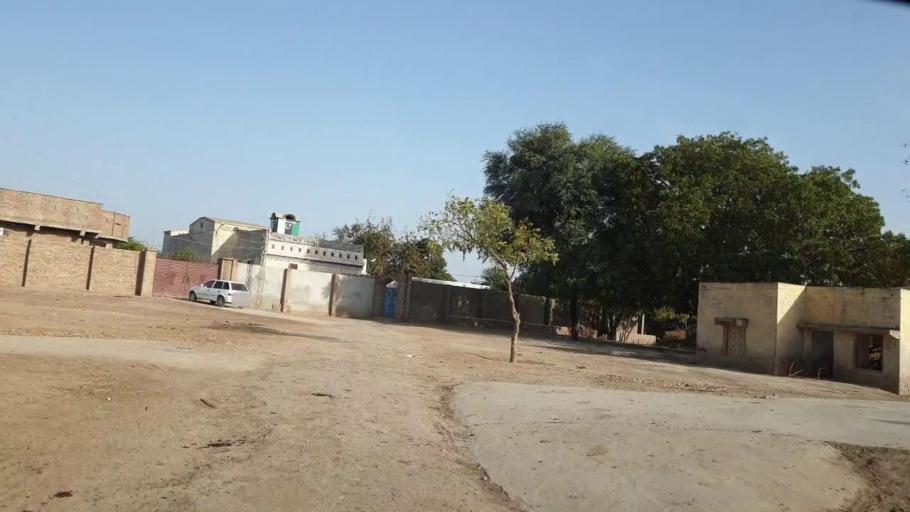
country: PK
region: Sindh
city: Kunri
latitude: 25.0740
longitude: 69.4361
